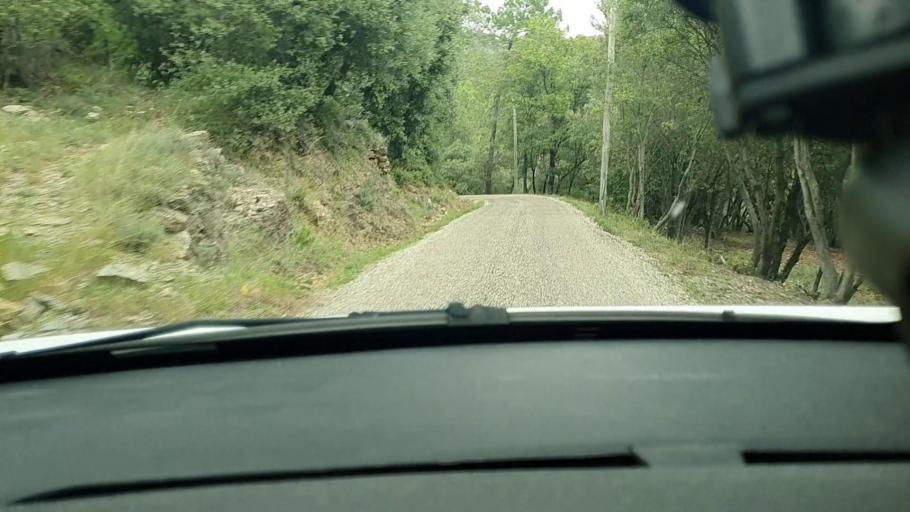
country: FR
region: Languedoc-Roussillon
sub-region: Departement du Gard
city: Branoux-les-Taillades
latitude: 44.2338
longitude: 3.9594
